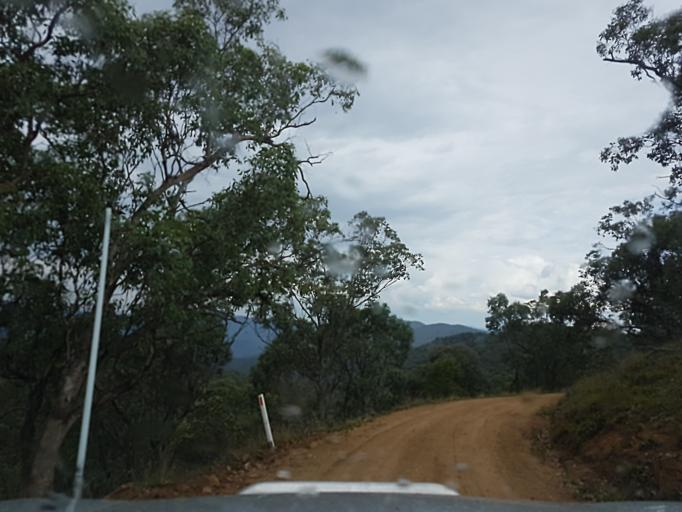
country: AU
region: New South Wales
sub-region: Snowy River
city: Jindabyne
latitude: -36.9441
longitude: 148.3474
